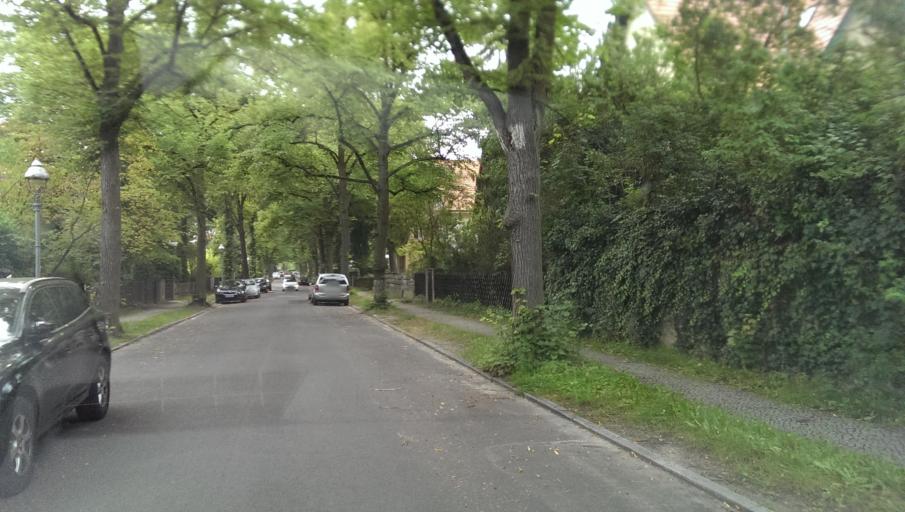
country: DE
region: Berlin
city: Zehlendorf Bezirk
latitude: 52.4393
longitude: 13.2599
